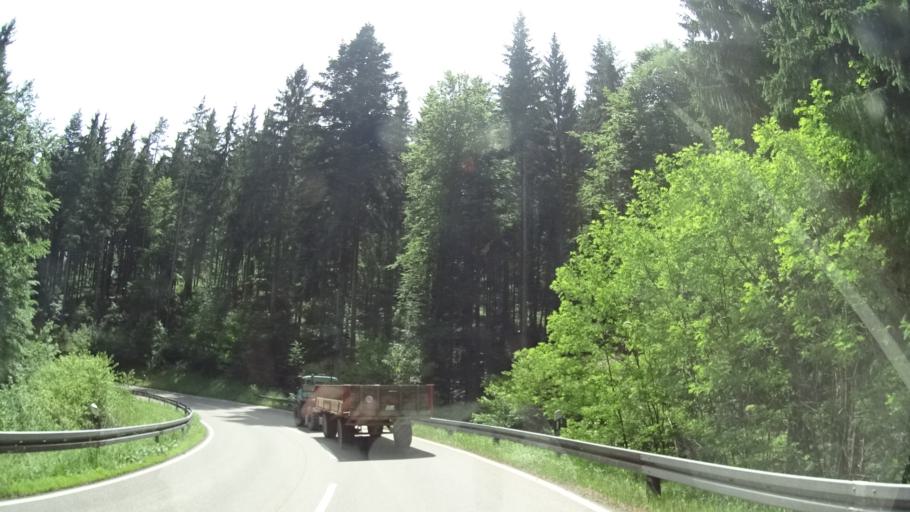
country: DE
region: Baden-Wuerttemberg
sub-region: Regierungsbezirk Stuttgart
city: Abtsgmund
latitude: 48.9104
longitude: 9.9923
